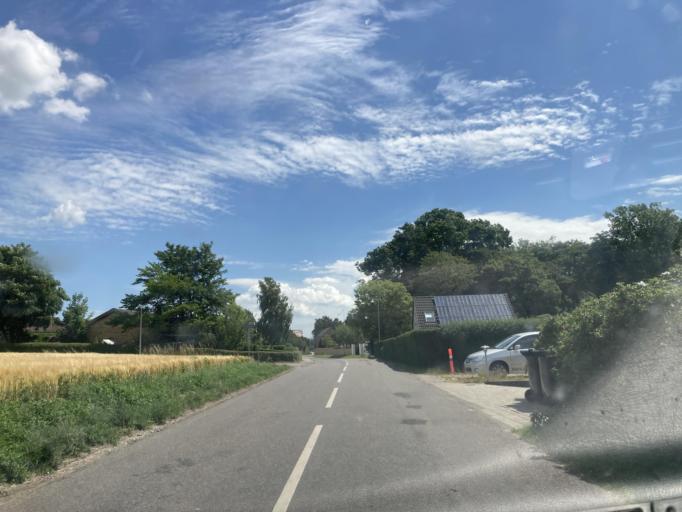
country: DK
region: Zealand
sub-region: Faxe Kommune
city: Haslev
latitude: 55.3767
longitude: 11.9622
